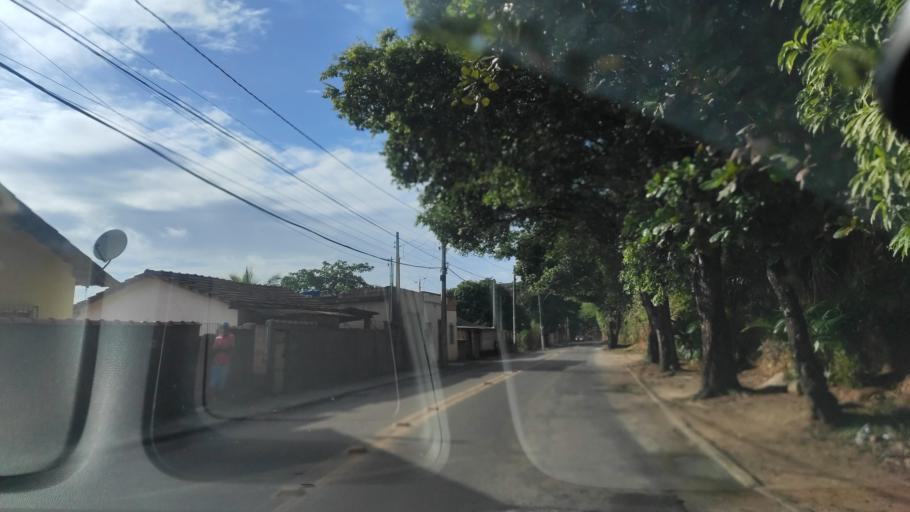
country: BR
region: Espirito Santo
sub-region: Nova Venecia
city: Nova Venecia
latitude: -18.7126
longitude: -40.3908
